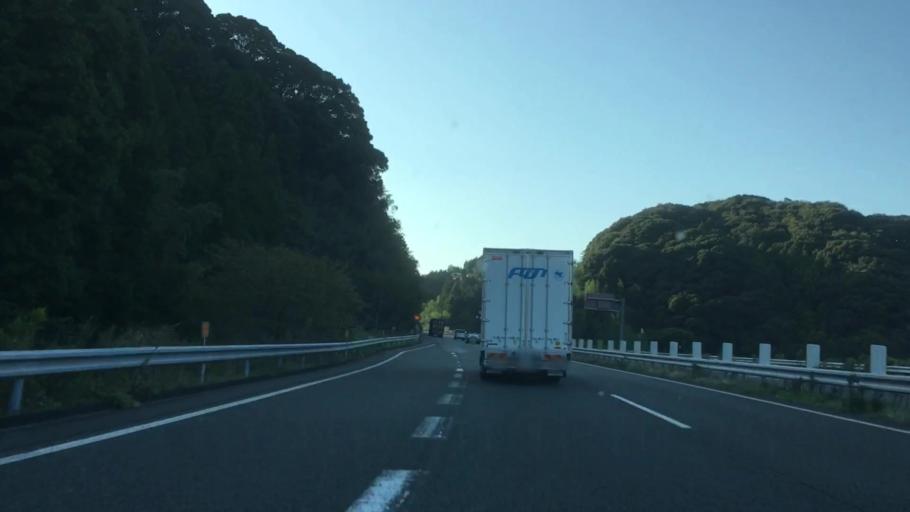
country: JP
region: Yamaguchi
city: Onoda
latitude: 34.1099
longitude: 131.1377
